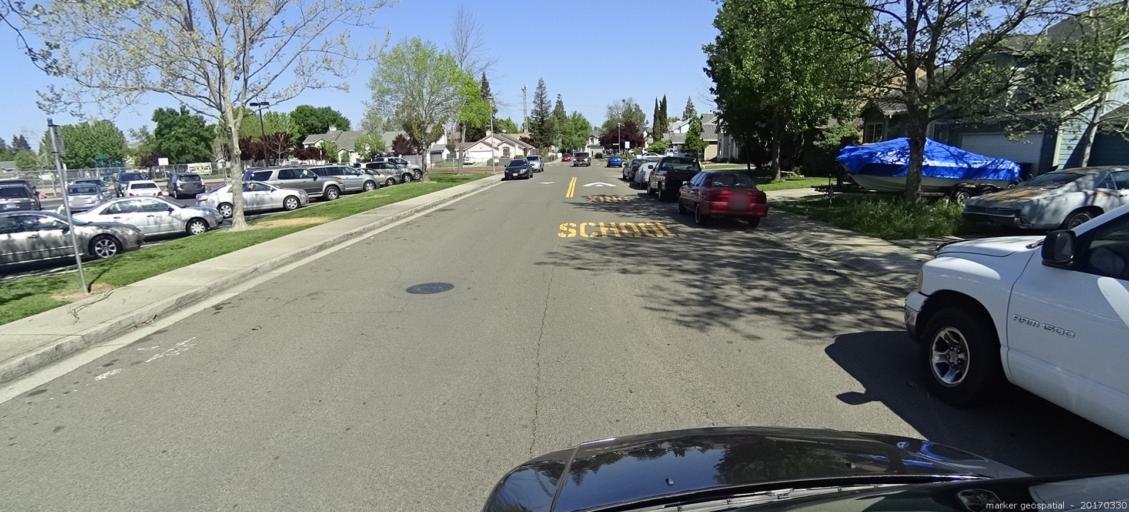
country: US
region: California
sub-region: Sacramento County
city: Laguna
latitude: 38.4469
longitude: -121.4207
